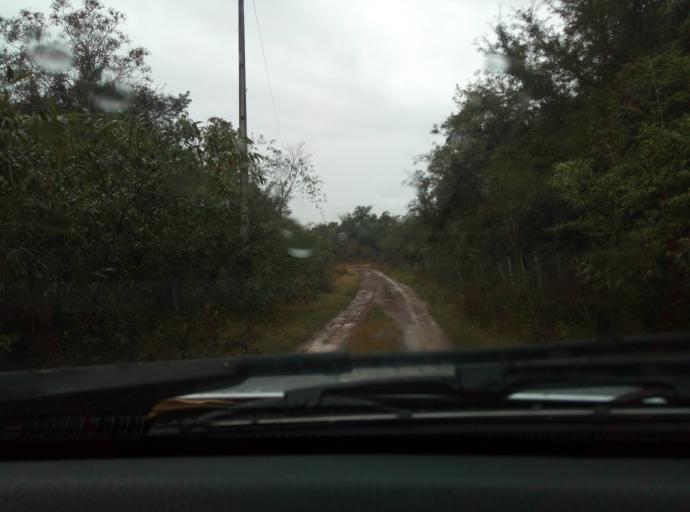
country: PY
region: Caaguazu
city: Carayao
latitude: -25.1066
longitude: -56.4137
